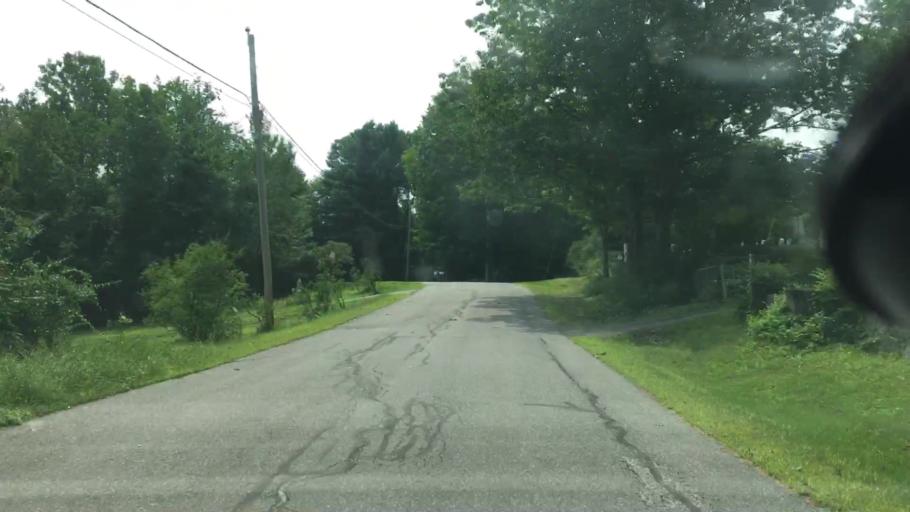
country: US
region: Maine
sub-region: Kennebec County
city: Wayne
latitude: 44.3407
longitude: -70.0677
